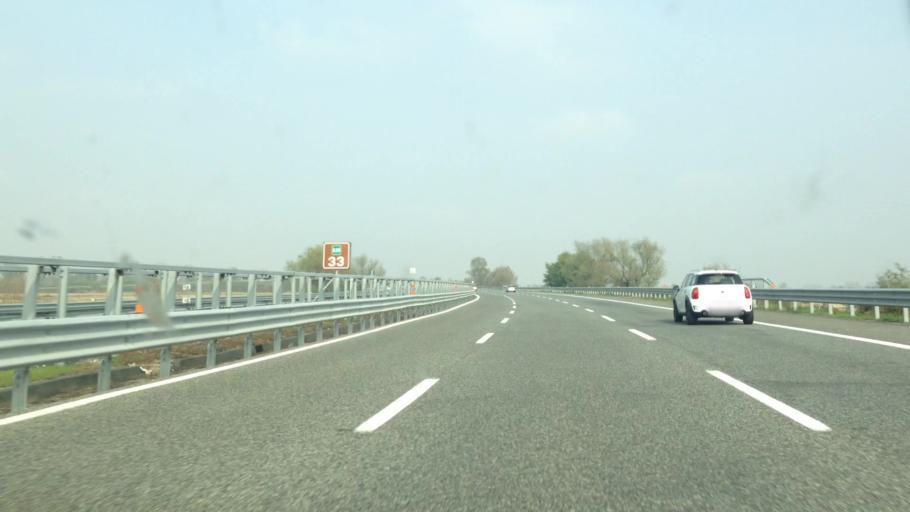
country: IT
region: Piedmont
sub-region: Provincia di Alessandria
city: Villanova Monferrato
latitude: 45.1854
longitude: 8.4971
